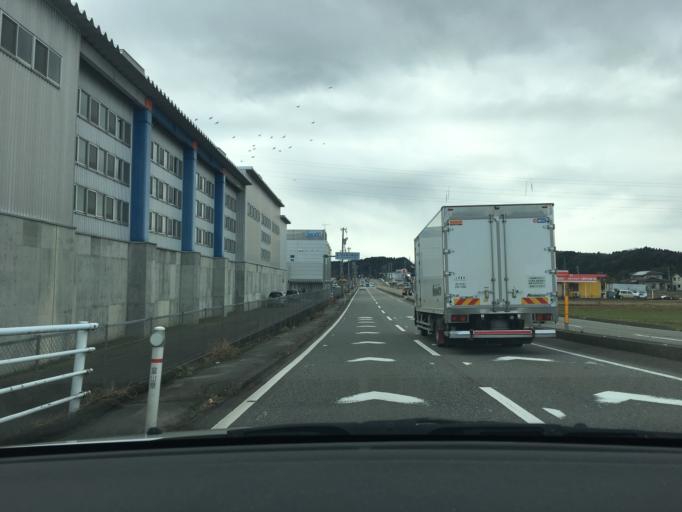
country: JP
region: Toyama
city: Toyama-shi
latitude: 36.6822
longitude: 137.1696
